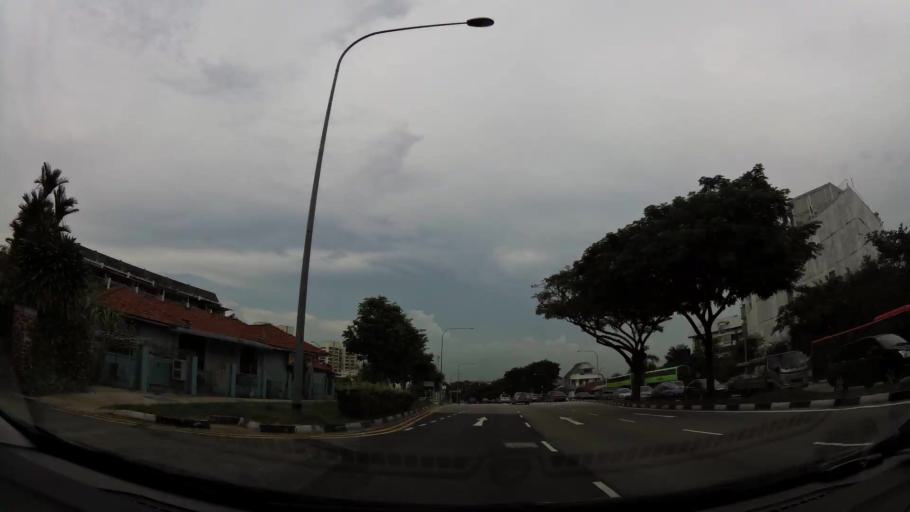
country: SG
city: Singapore
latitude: 1.3629
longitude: 103.8734
